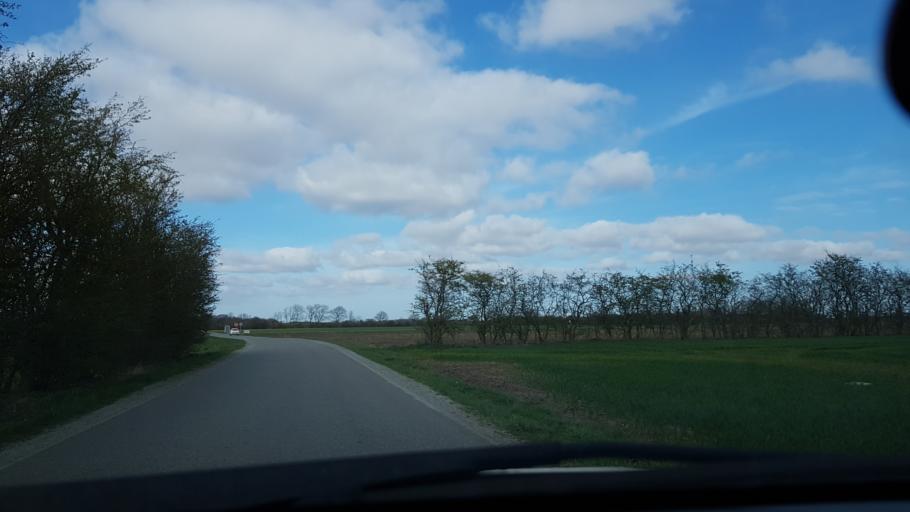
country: DK
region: South Denmark
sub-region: Vejen Kommune
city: Rodding
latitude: 55.3946
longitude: 9.0100
